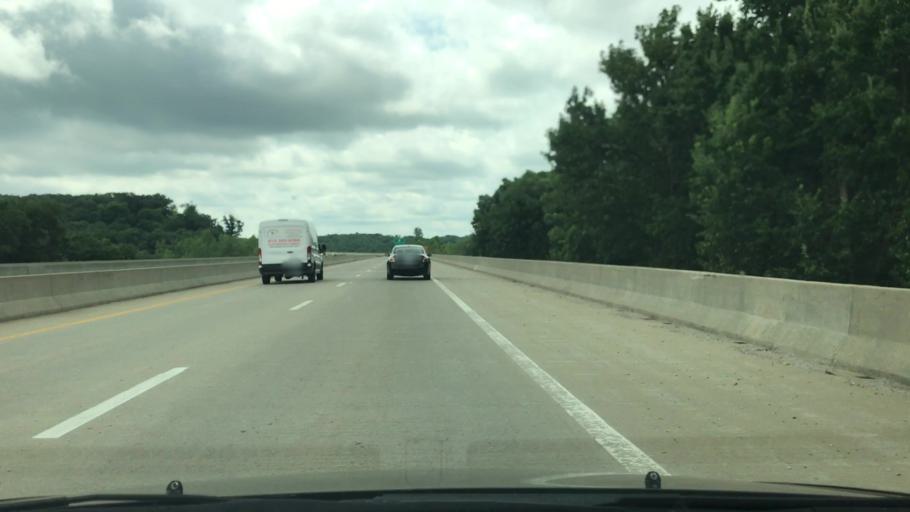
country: US
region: Missouri
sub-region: Jackson County
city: Grandview
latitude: 38.8695
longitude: -94.6018
